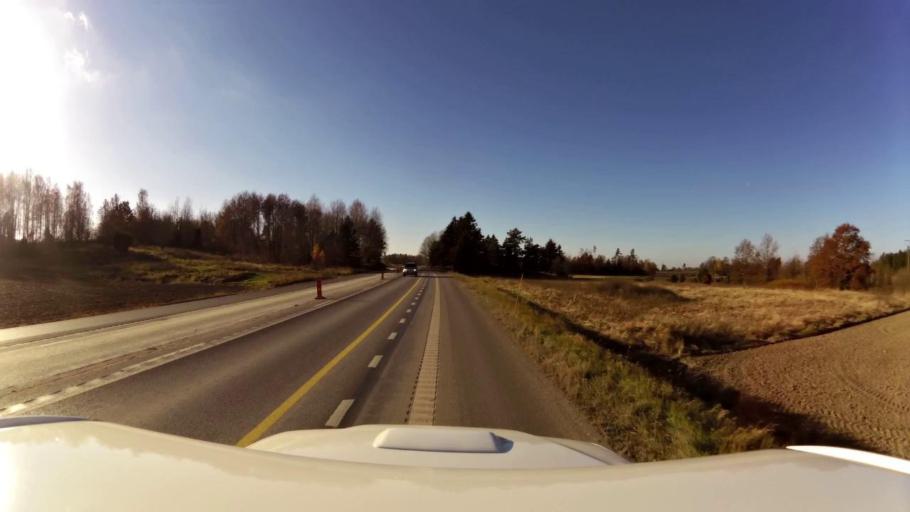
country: SE
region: OEstergoetland
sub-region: Linkopings Kommun
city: Linghem
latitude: 58.4364
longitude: 15.7392
